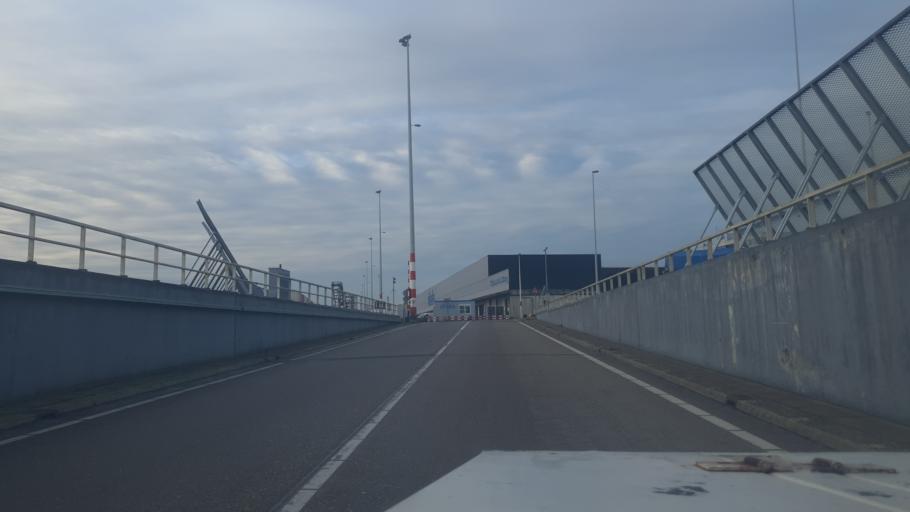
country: NL
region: North Holland
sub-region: Gemeente Aalsmeer
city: Aalsmeer
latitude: 52.2981
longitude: 4.7505
